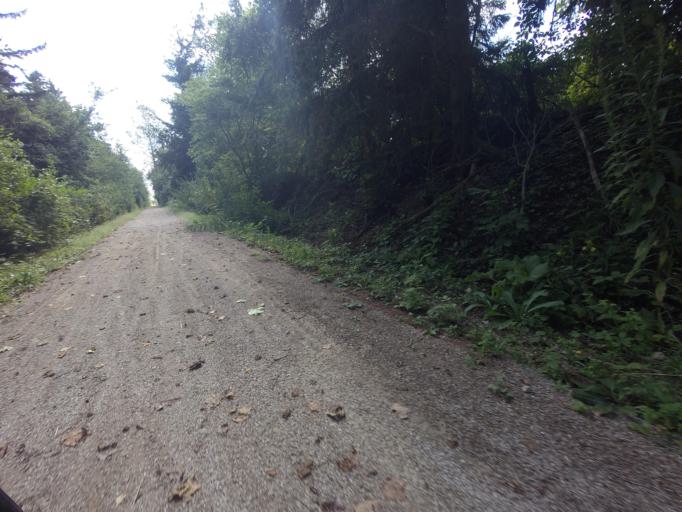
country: CA
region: Ontario
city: Huron East
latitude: 43.6548
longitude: -81.2379
